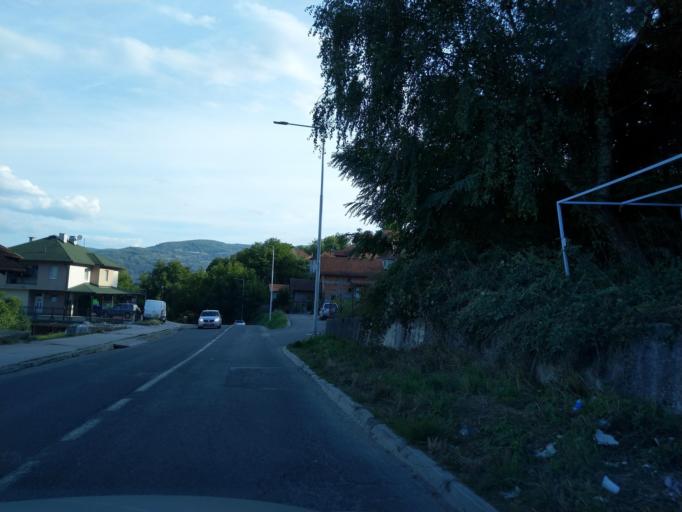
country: RS
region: Central Serbia
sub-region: Zlatiborski Okrug
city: Prijepolje
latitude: 43.3542
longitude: 19.6356
